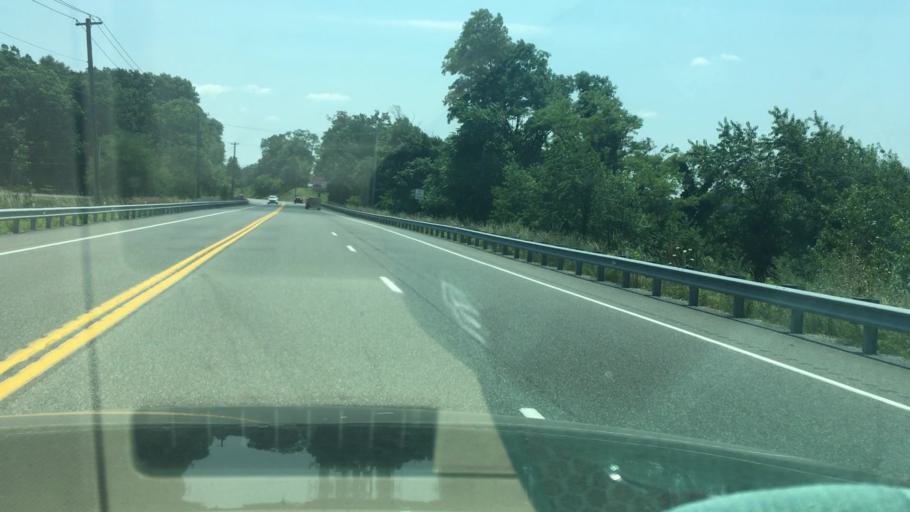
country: US
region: Pennsylvania
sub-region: Lehigh County
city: Schnecksville
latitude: 40.6178
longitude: -75.6593
